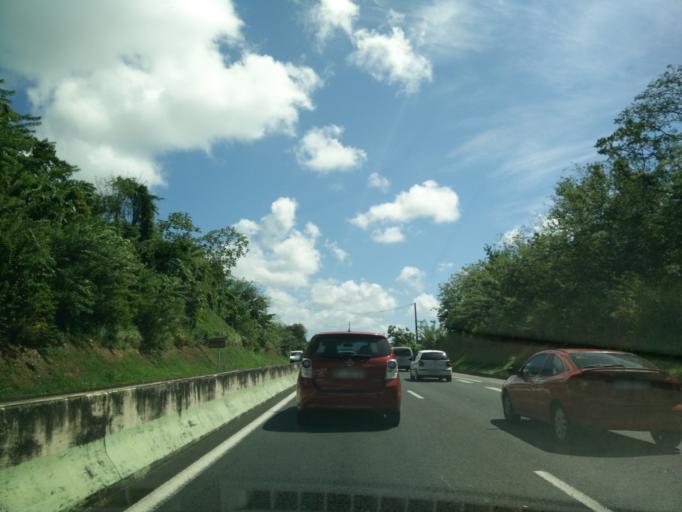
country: MQ
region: Martinique
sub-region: Martinique
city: Ducos
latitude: 14.5798
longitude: -60.9820
